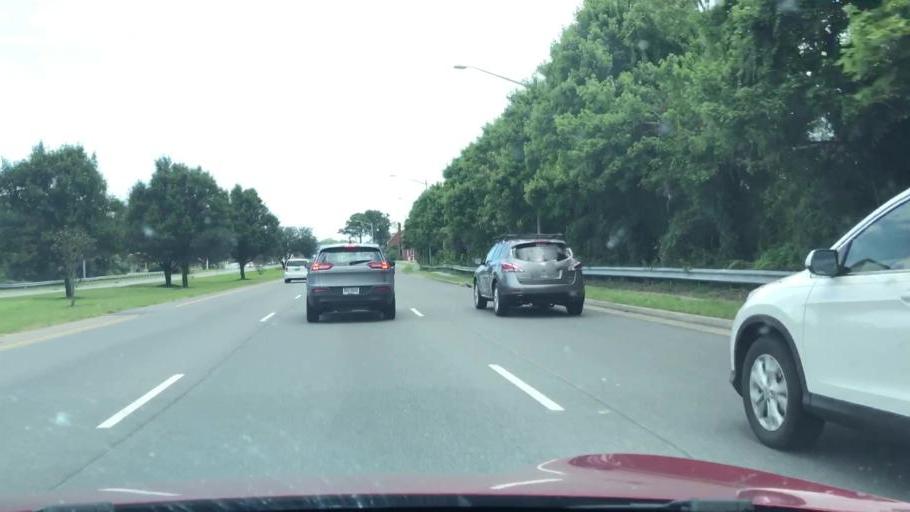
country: US
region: Virginia
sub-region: City of Chesapeake
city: Chesapeake
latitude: 36.8595
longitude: -76.1330
